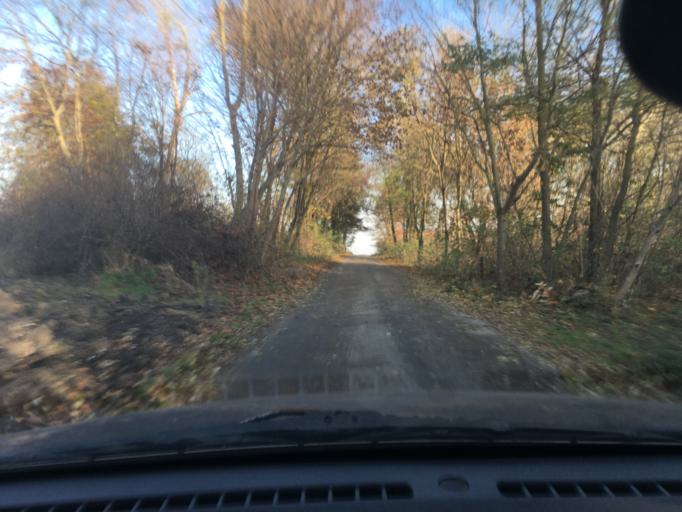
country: PL
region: Masovian Voivodeship
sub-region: Powiat plocki
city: Mala Wies
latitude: 52.4435
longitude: 20.1015
